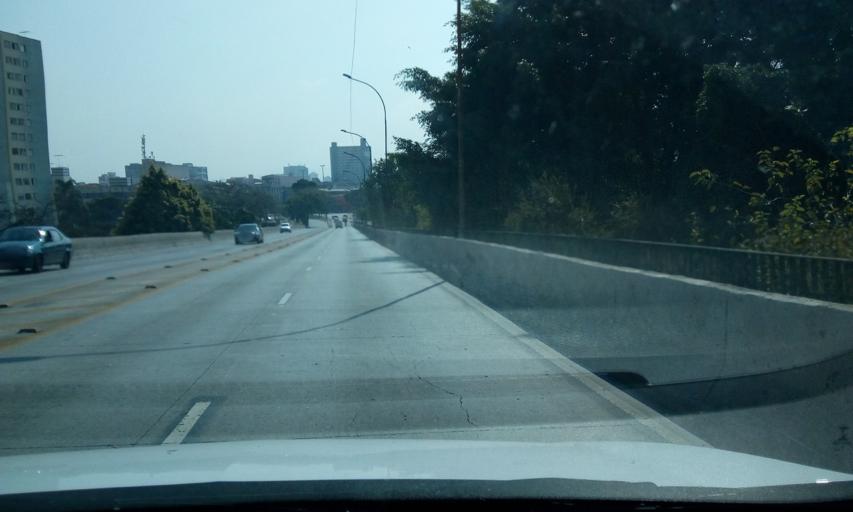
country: BR
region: Sao Paulo
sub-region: Sao Paulo
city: Sao Paulo
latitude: -23.5452
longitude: -46.6048
